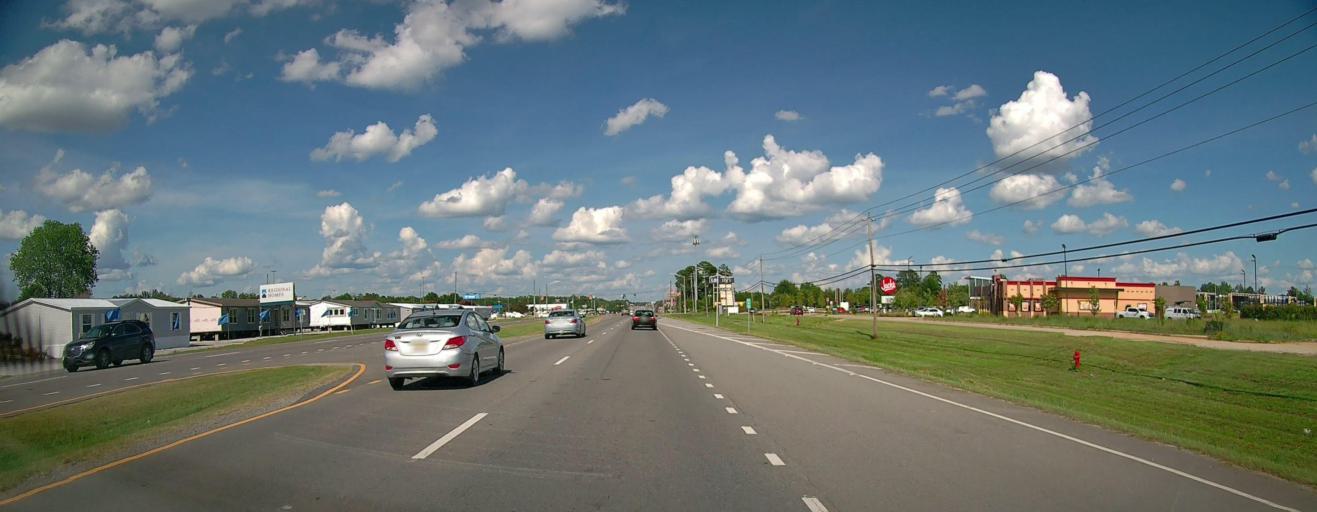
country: US
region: Alabama
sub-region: Tuscaloosa County
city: Northport
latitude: 33.2341
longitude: -87.6172
